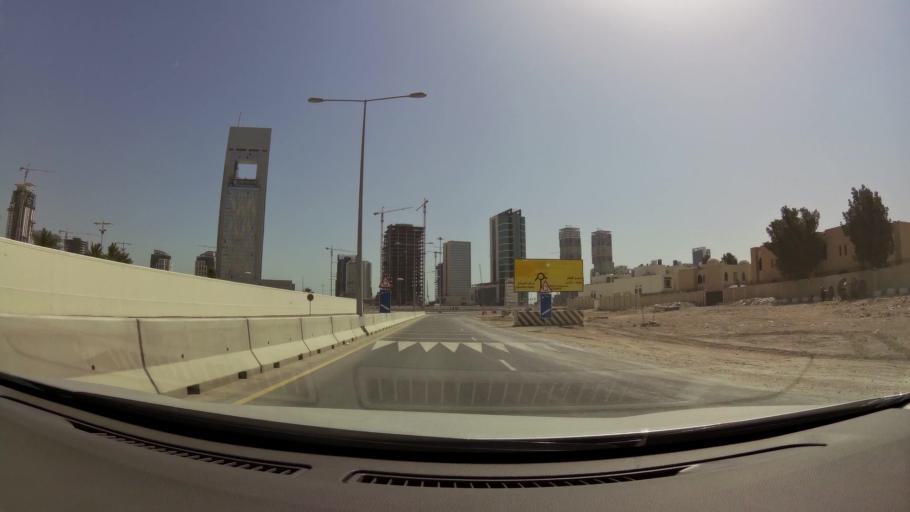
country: QA
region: Baladiyat ad Dawhah
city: Doha
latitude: 25.3897
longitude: 51.5161
